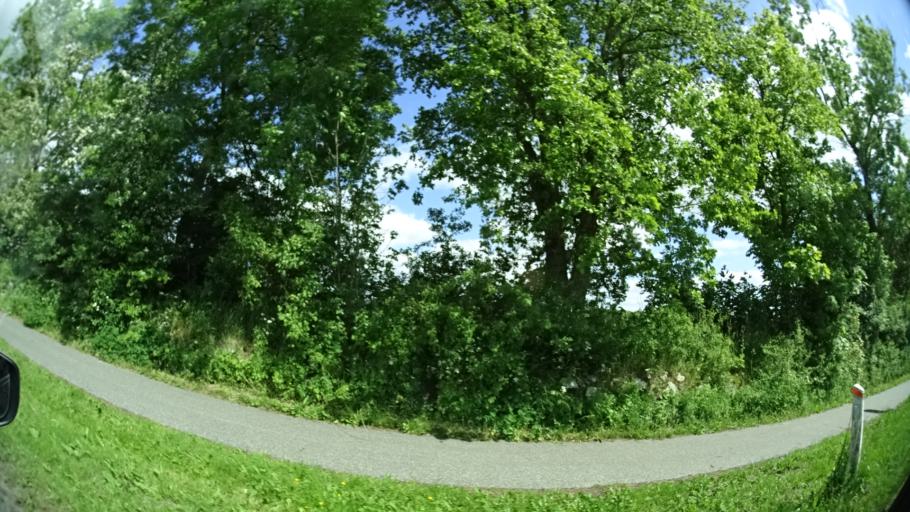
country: DK
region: Central Jutland
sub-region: Syddjurs Kommune
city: Ronde
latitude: 56.2942
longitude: 10.4814
